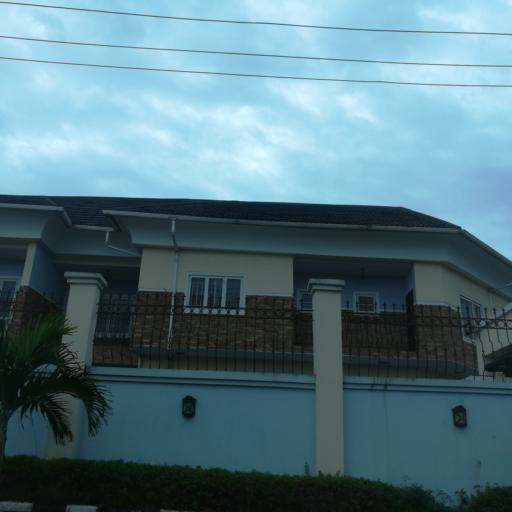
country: NG
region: Lagos
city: Ikoyi
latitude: 6.4378
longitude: 3.4684
